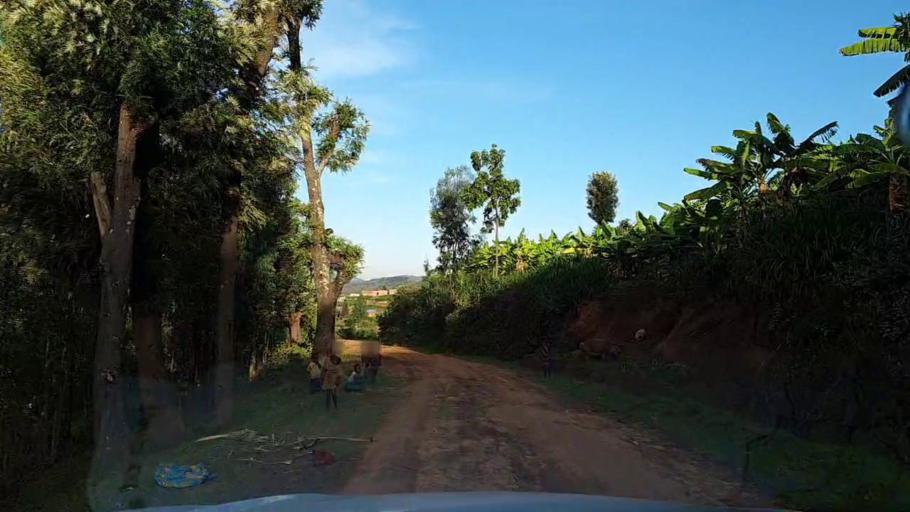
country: RW
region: Southern Province
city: Gikongoro
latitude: -2.4037
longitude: 29.5530
